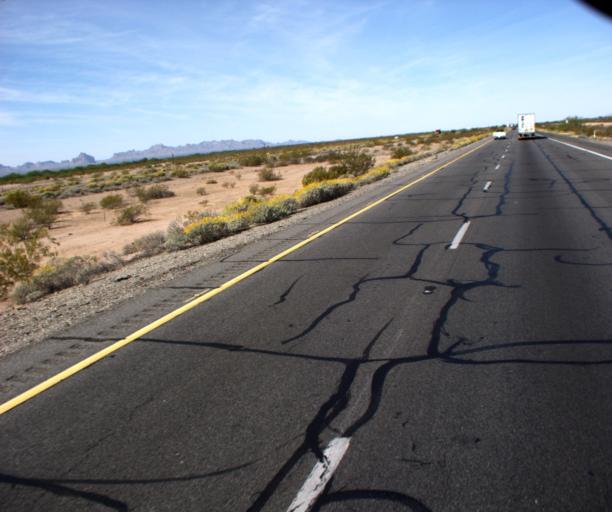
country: US
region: Arizona
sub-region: La Paz County
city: Salome
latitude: 33.5397
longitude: -113.1631
